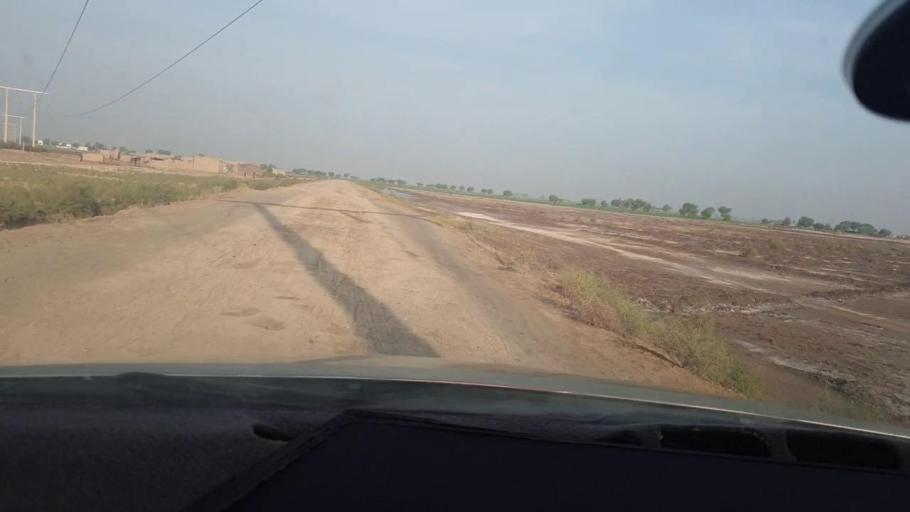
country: PK
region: Sindh
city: Jacobabad
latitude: 28.3352
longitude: 68.4104
